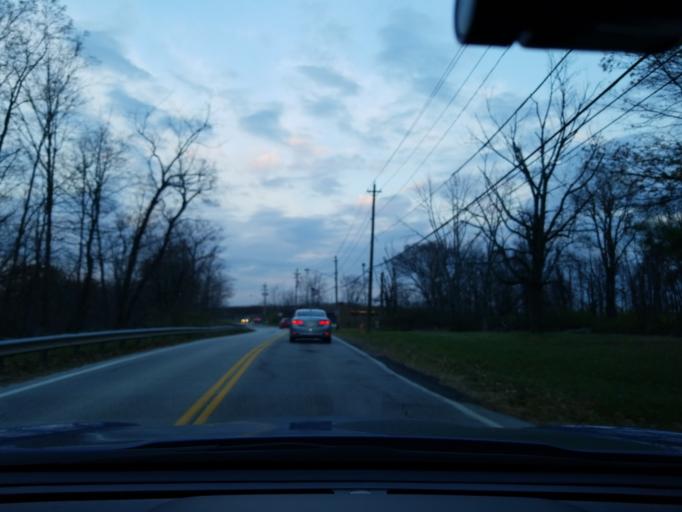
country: US
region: Ohio
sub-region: Cuyahoga County
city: Berea
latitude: 41.3924
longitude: -81.8686
